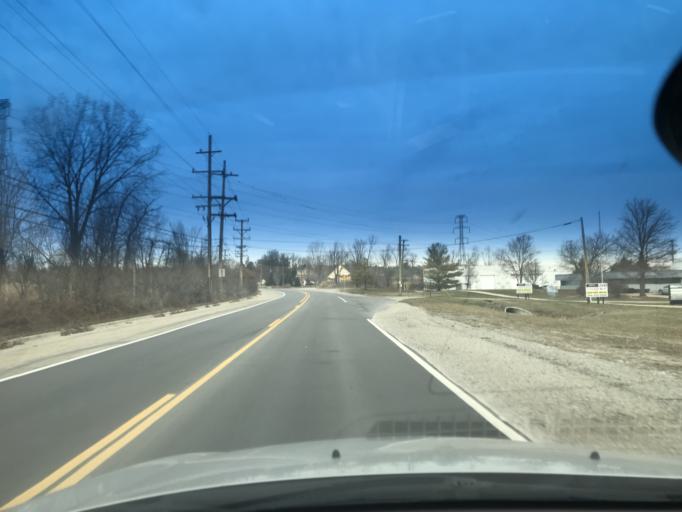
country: US
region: Michigan
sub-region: Macomb County
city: Shelby
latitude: 42.7098
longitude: -83.0549
